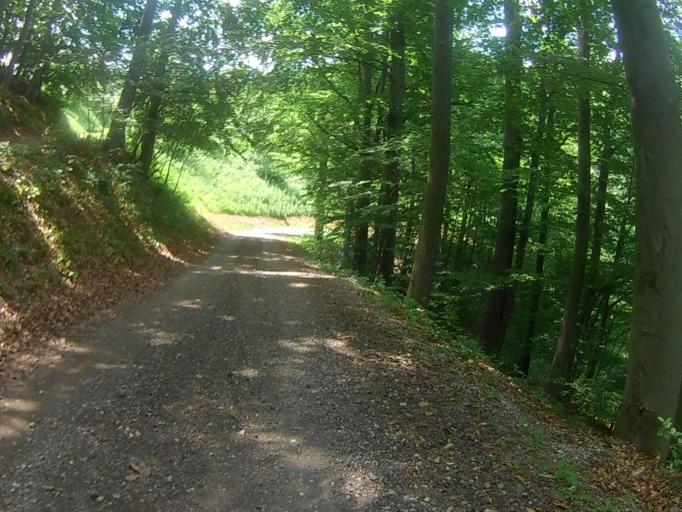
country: SI
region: Kungota
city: Zgornja Kungota
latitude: 46.6212
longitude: 15.6140
